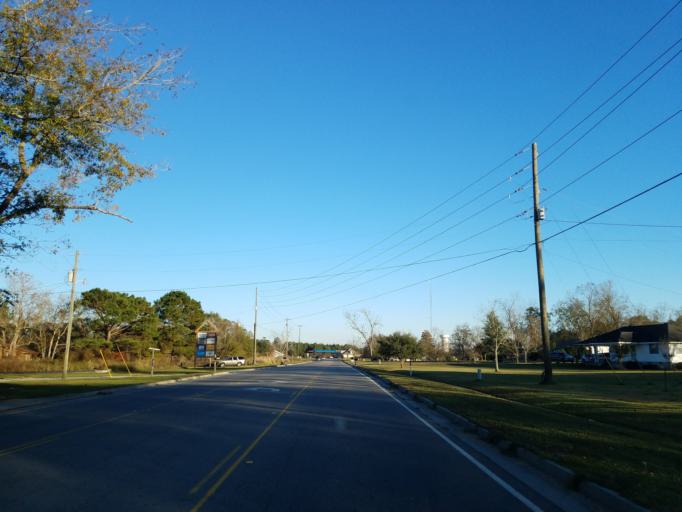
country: US
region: Mississippi
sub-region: Lamar County
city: Arnold Line
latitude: 31.3338
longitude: -89.3854
